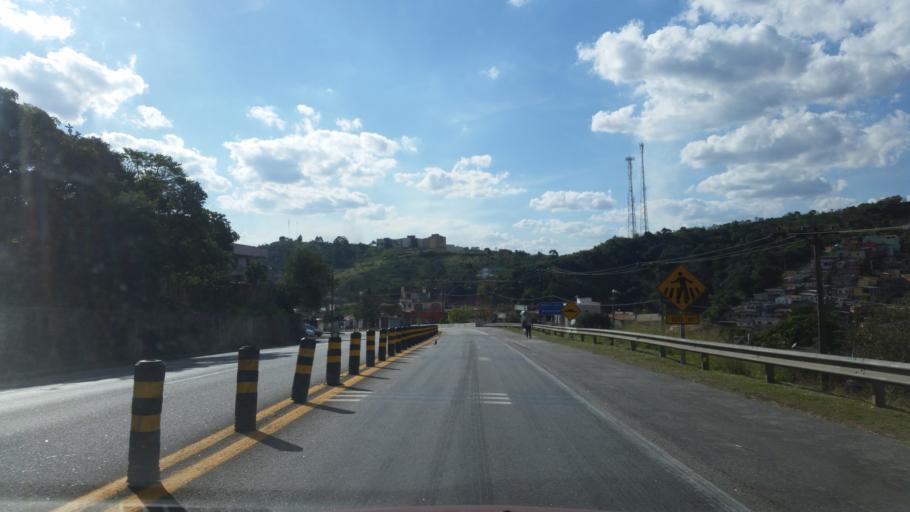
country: BR
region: Sao Paulo
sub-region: Mairinque
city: Mairinque
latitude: -23.5229
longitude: -47.2534
